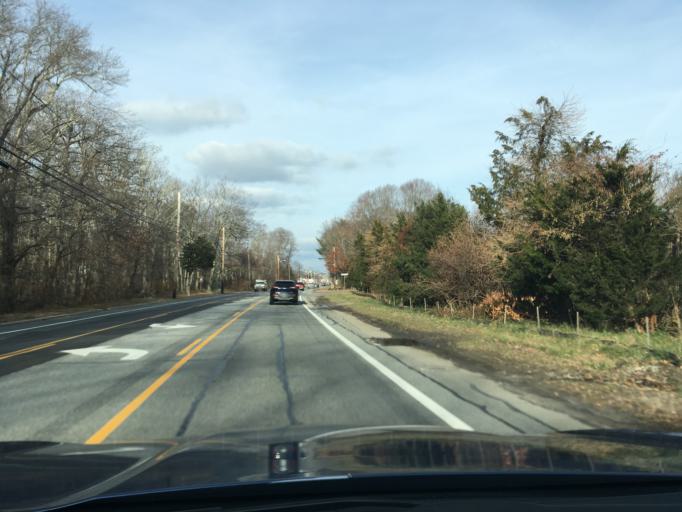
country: US
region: Rhode Island
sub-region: Washington County
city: North Kingstown
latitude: 41.5811
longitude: -71.4597
